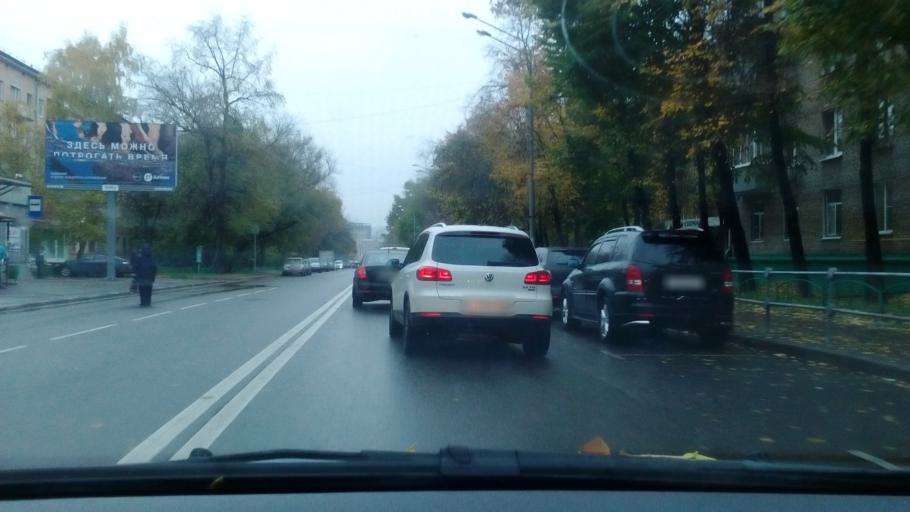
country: RU
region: Moscow
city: Mar'ina Roshcha
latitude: 55.7974
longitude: 37.5762
